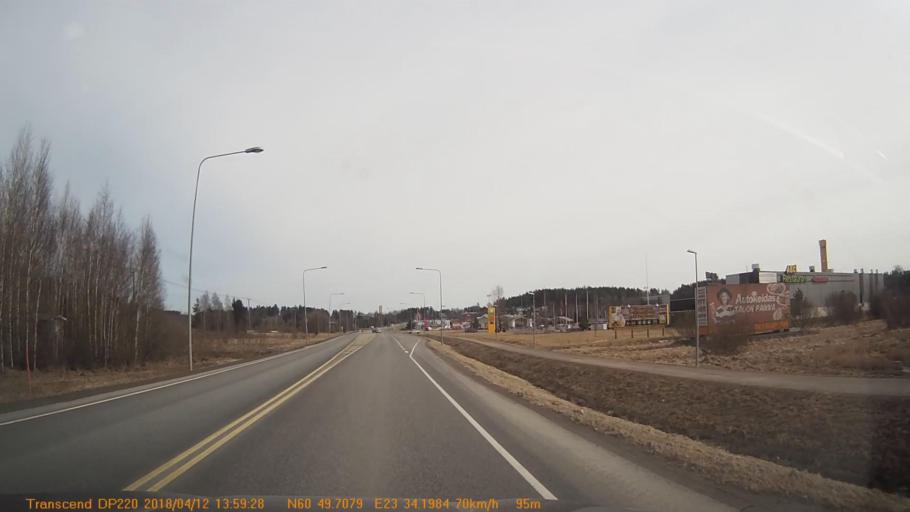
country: FI
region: Haeme
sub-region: Forssa
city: Forssa
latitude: 60.8284
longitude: 23.5702
